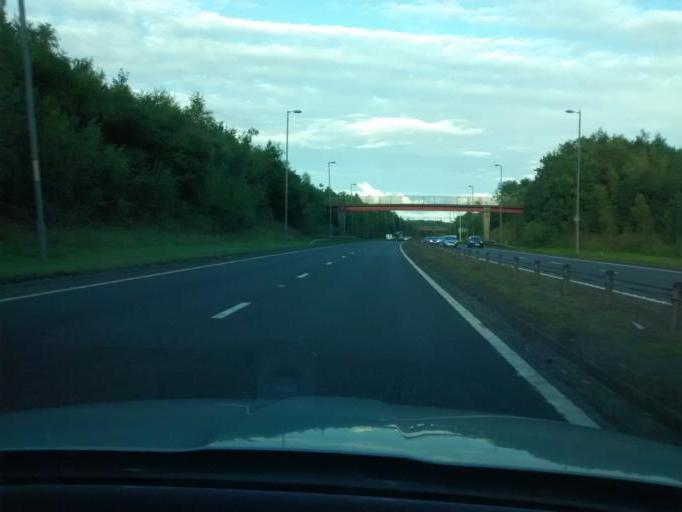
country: GB
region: Scotland
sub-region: Renfrewshire
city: Johnstone
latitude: 55.8424
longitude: -4.5063
